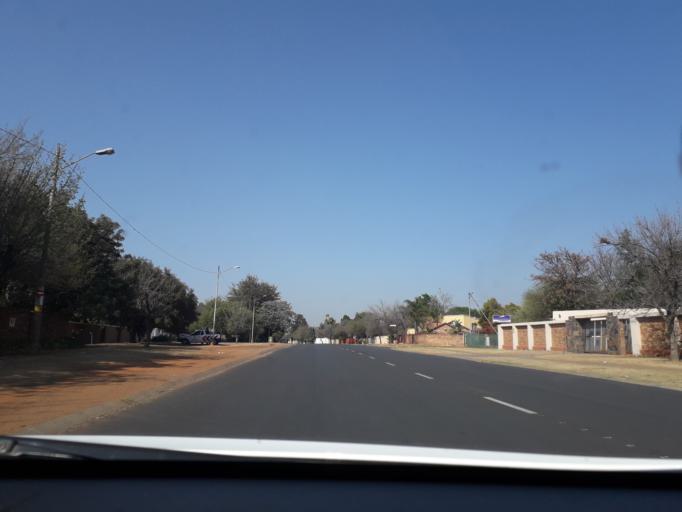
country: ZA
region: Gauteng
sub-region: City of Johannesburg Metropolitan Municipality
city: Modderfontein
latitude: -26.0947
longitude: 28.2421
